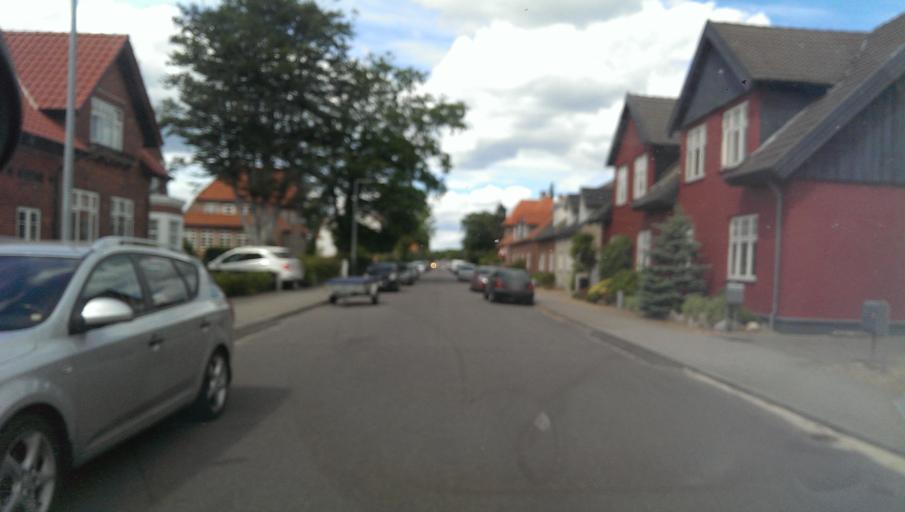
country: DK
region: South Denmark
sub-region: Esbjerg Kommune
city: Esbjerg
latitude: 55.4762
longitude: 8.4524
